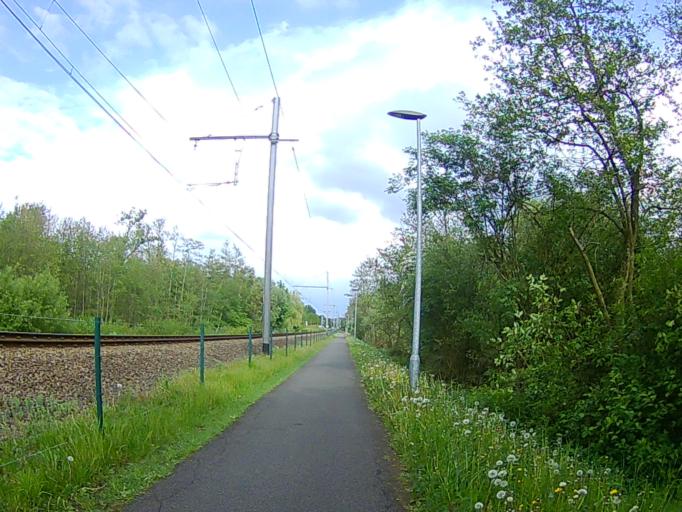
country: BE
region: Flanders
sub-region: Provincie Antwerpen
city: Niel
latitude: 51.0814
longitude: 4.3342
